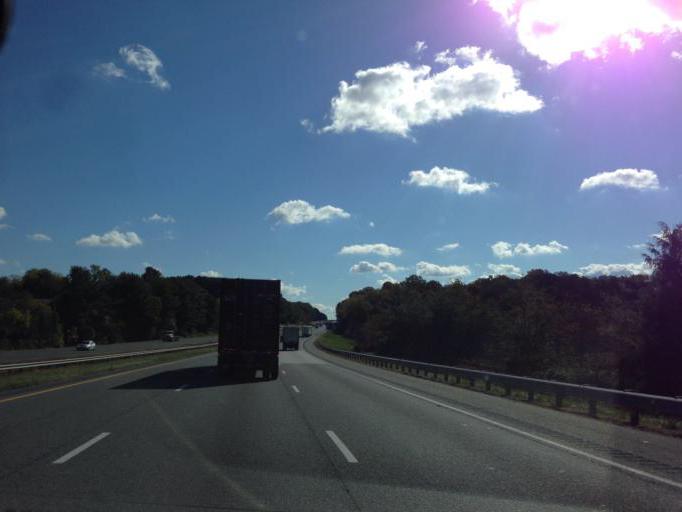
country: US
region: Maryland
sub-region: Carroll County
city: Sykesville
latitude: 39.3363
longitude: -77.0426
